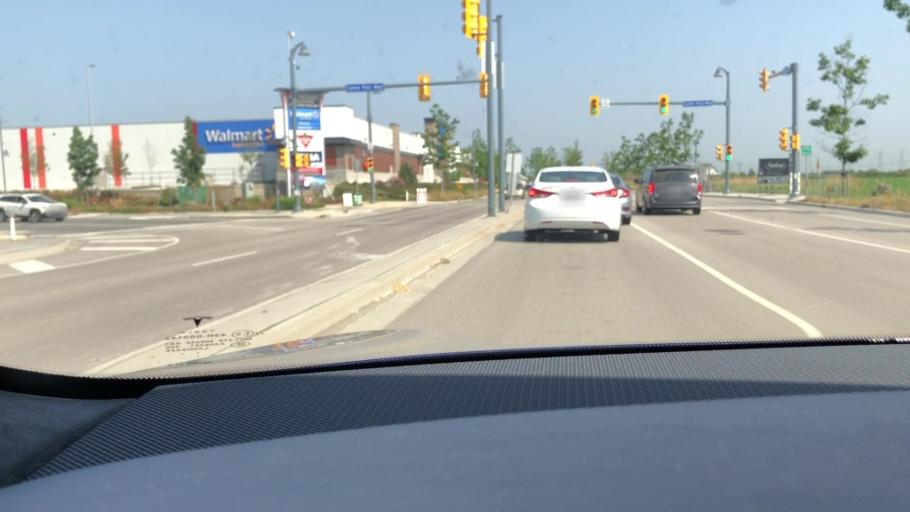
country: CA
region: British Columbia
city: Ladner
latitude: 49.0410
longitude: -123.0798
